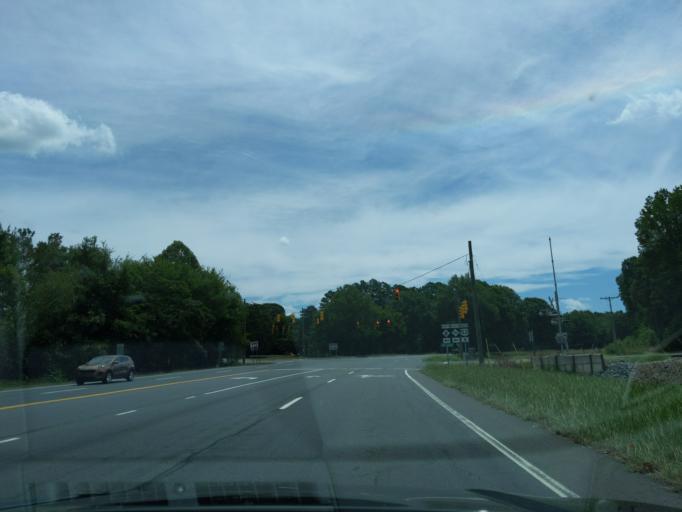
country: US
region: North Carolina
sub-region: Stanly County
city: Albemarle
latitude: 35.4443
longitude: -80.2243
